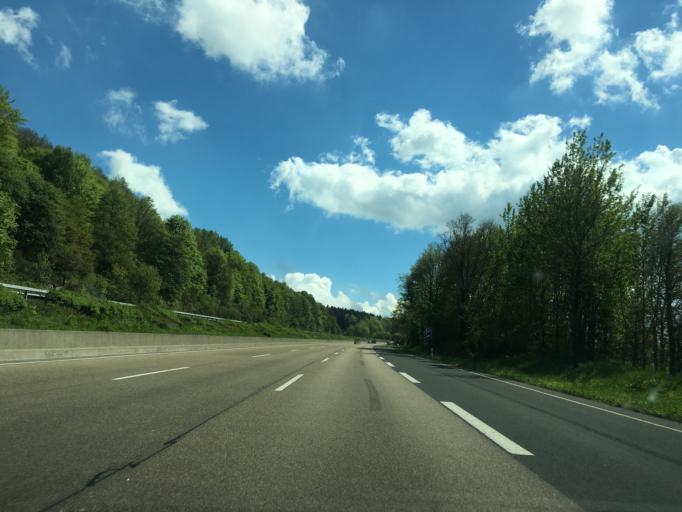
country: DE
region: Bavaria
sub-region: Regierungsbezirk Unterfranken
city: Motten
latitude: 50.3873
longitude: 9.7338
